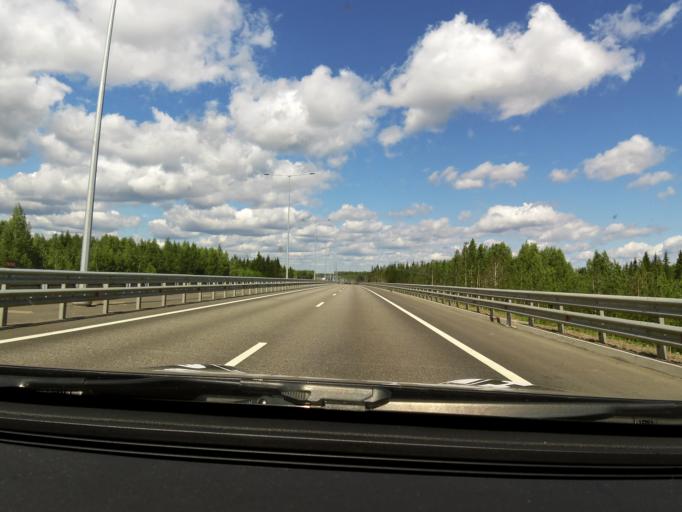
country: RU
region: Tverskaya
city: Vyshniy Volochek
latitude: 57.4004
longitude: 34.5365
